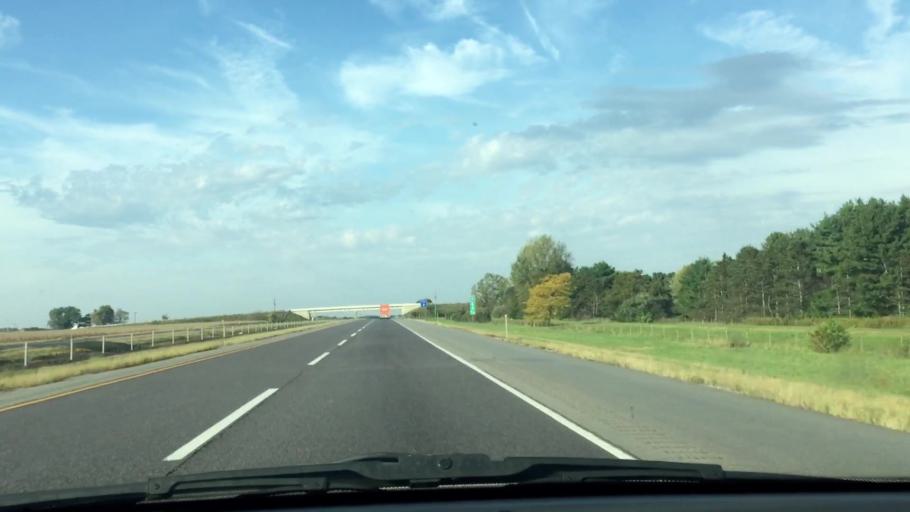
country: US
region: Illinois
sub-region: Lee County
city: Franklin Grove
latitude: 41.8366
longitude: -89.2701
